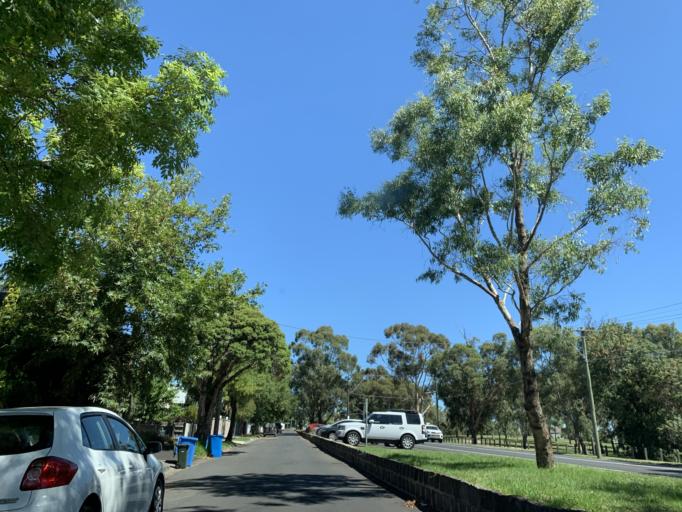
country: AU
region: Victoria
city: Ripponlea
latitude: -37.8899
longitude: 144.9961
